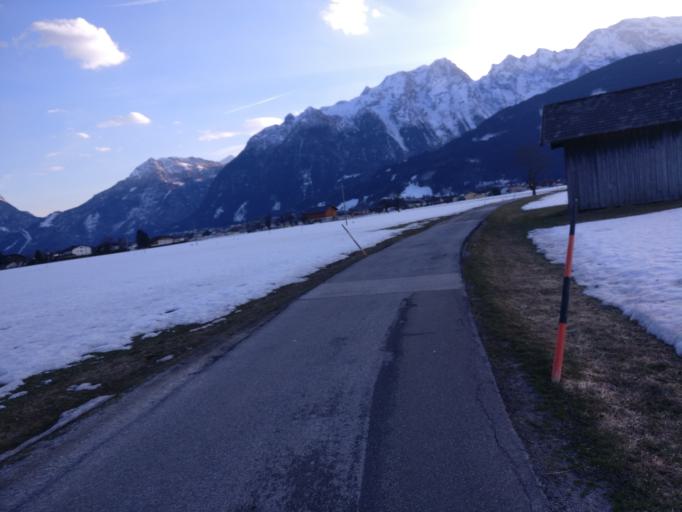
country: AT
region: Salzburg
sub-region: Politischer Bezirk Hallein
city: Kuchl
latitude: 47.6446
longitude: 13.1535
